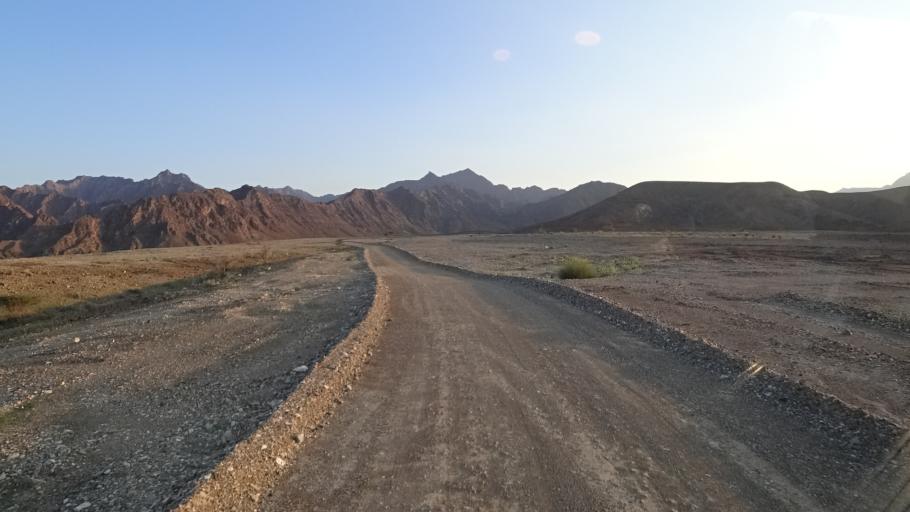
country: OM
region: Al Batinah
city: Al Khaburah
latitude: 23.7521
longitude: 56.9239
